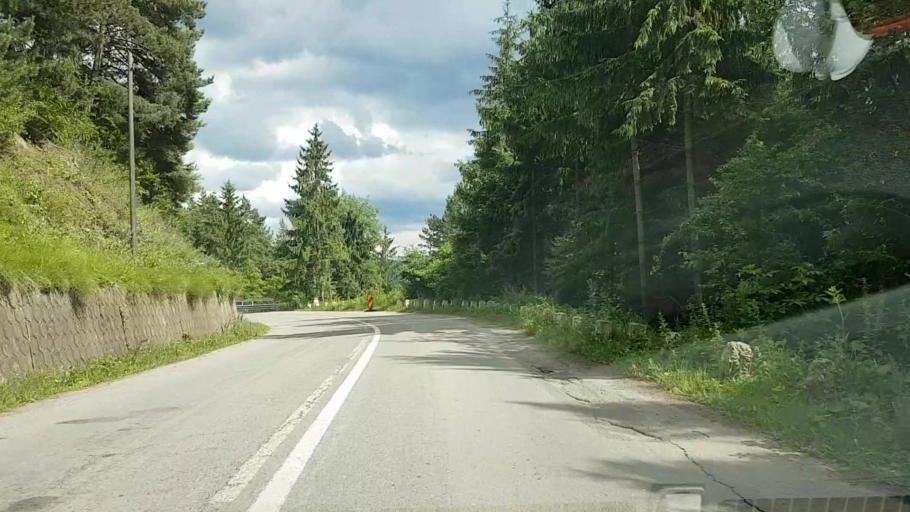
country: RO
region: Neamt
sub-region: Comuna Hangu
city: Hangu
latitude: 47.0480
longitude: 26.0131
